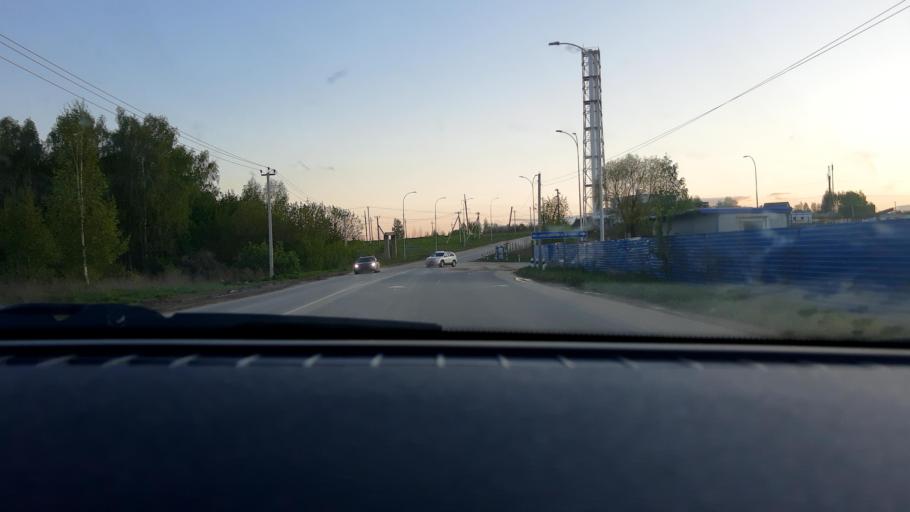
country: RU
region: Nizjnij Novgorod
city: Afonino
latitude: 56.2432
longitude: 44.0619
